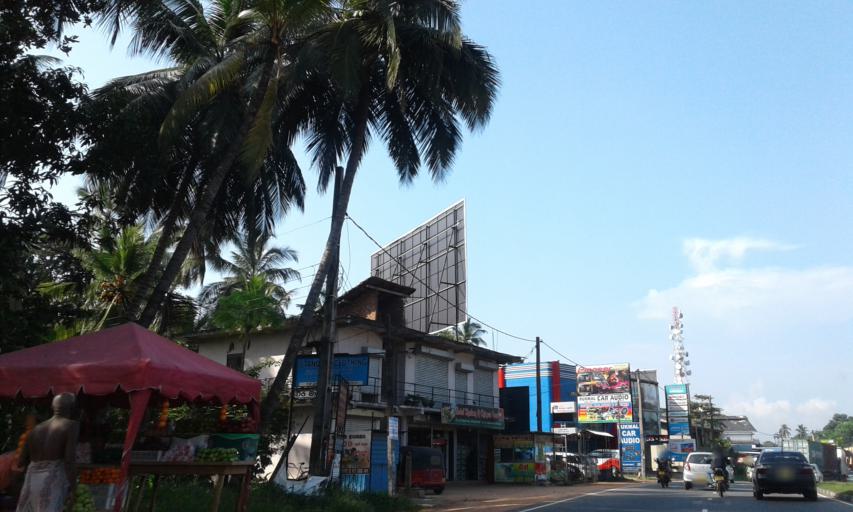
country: LK
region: Western
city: Gampaha
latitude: 7.0223
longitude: 79.9757
